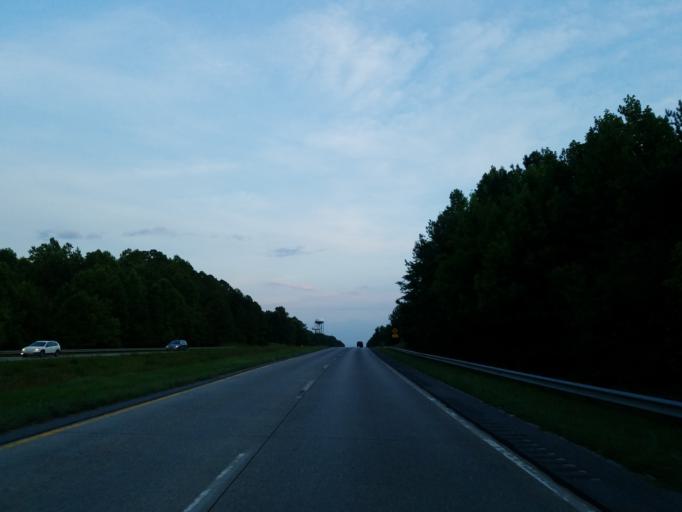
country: US
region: Georgia
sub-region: Pickens County
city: Jasper
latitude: 34.4340
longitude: -84.4358
